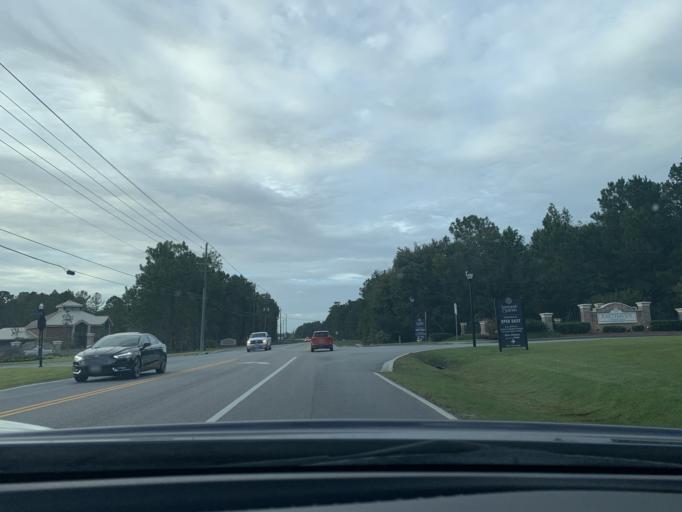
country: US
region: Georgia
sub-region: Chatham County
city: Pooler
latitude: 32.0662
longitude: -81.2738
